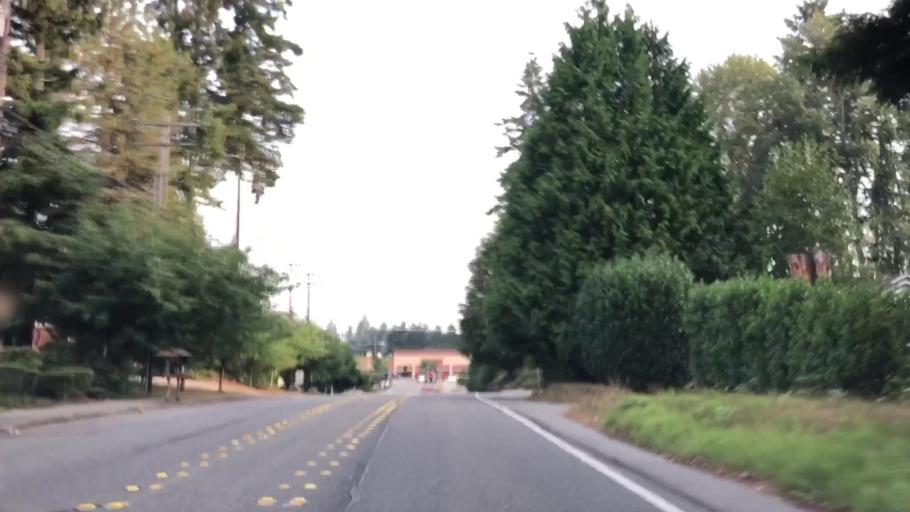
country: US
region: Washington
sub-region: King County
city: Bothell
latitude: 47.7899
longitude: -122.2131
